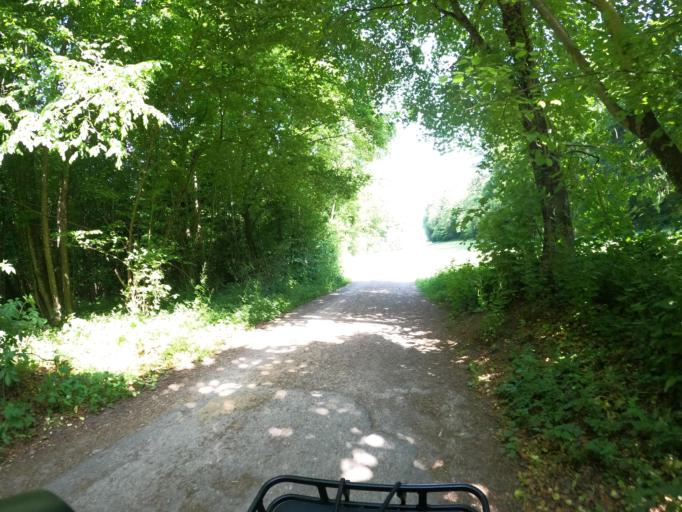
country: CH
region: Zurich
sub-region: Bezirk Dielsdorf
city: Niederglatt
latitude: 47.4881
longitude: 8.4912
